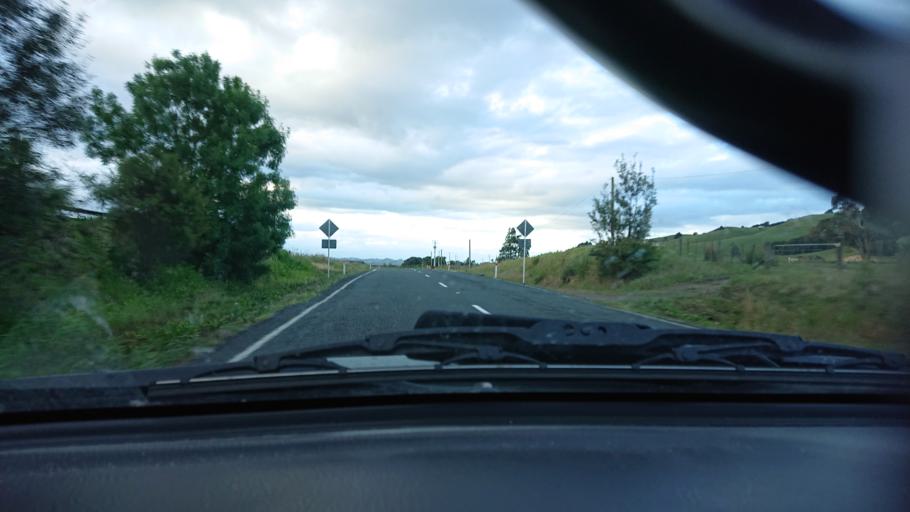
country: NZ
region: Auckland
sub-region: Auckland
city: Wellsford
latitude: -36.4540
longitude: 174.4353
